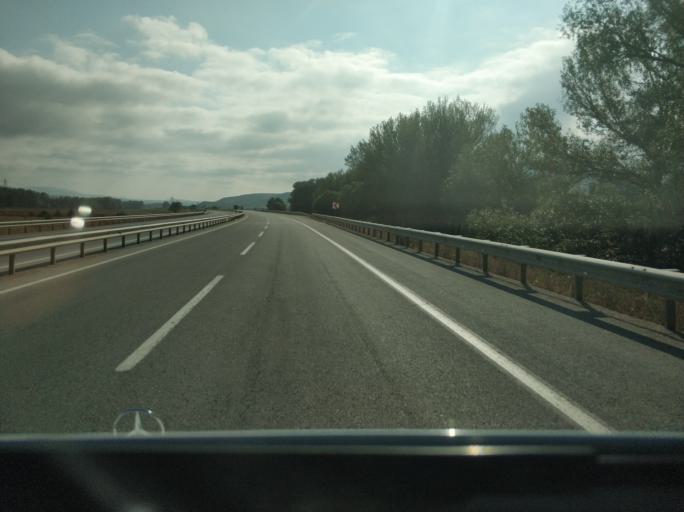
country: TR
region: Sivas
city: Yildizeli
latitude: 39.8483
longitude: 36.5240
